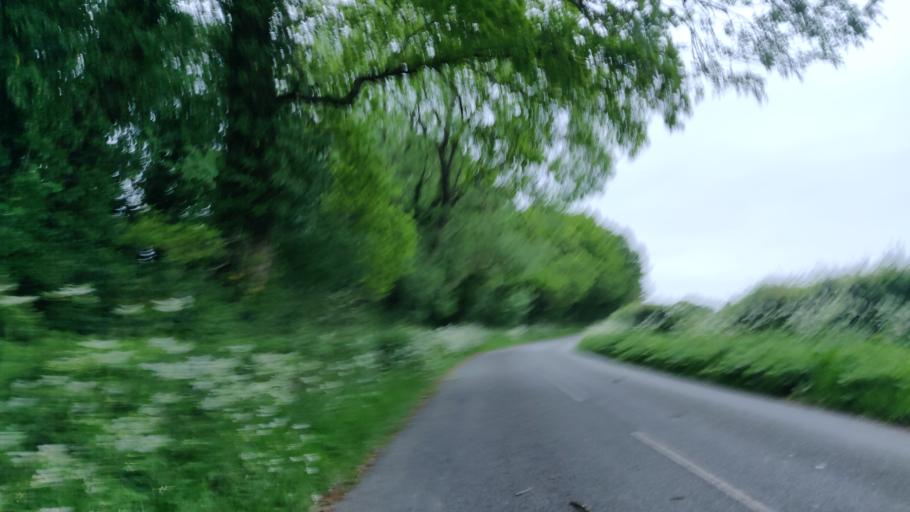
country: GB
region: England
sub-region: West Sussex
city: Southwater
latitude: 51.0285
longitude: -0.3680
